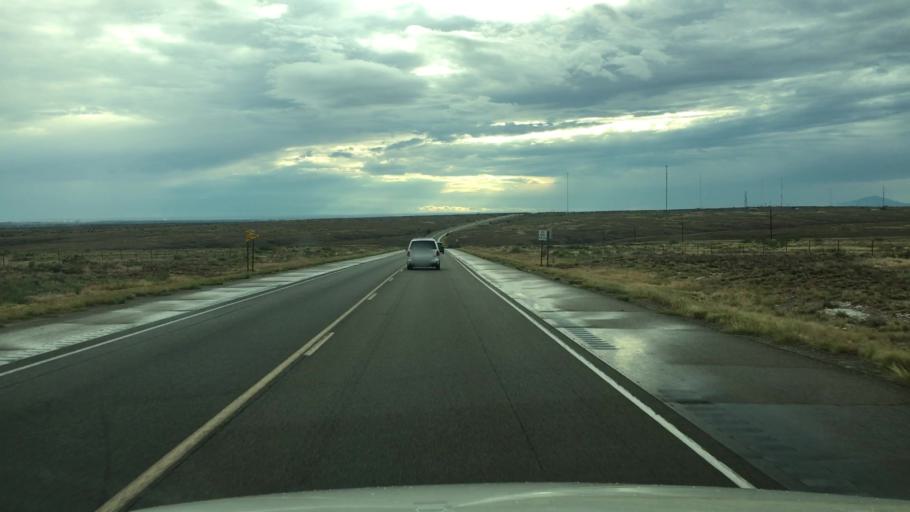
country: US
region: New Mexico
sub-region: Chaves County
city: Roswell
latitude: 33.3982
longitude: -104.3534
